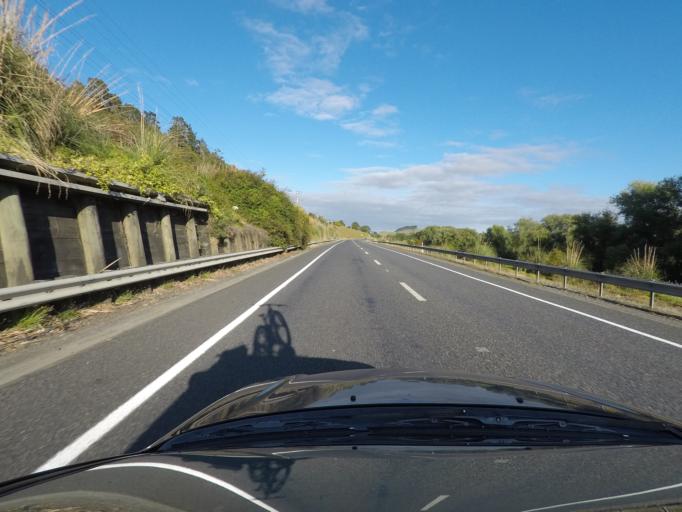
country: NZ
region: Northland
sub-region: Far North District
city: Kawakawa
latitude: -35.5277
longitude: 174.2205
